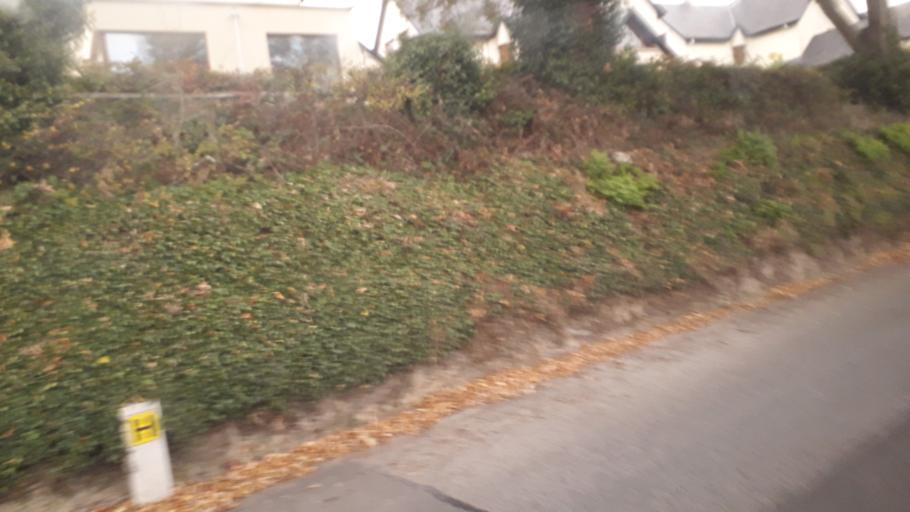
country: IE
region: Munster
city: Ballina
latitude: 52.8063
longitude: -8.4351
